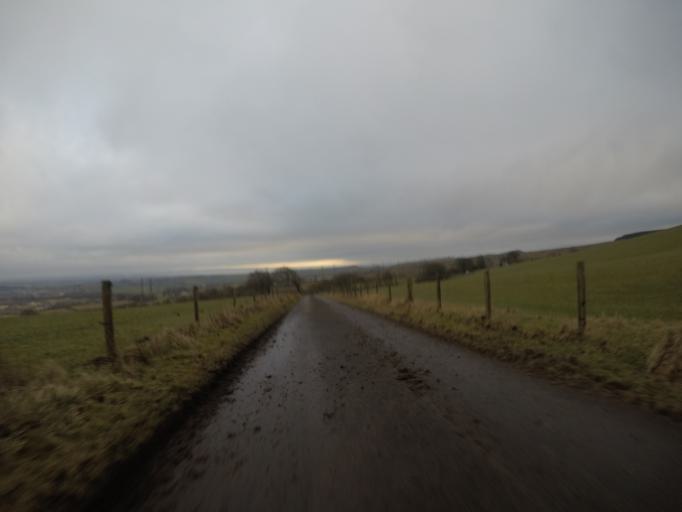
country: GB
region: Scotland
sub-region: North Ayrshire
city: Dalry
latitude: 55.7268
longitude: -4.7638
